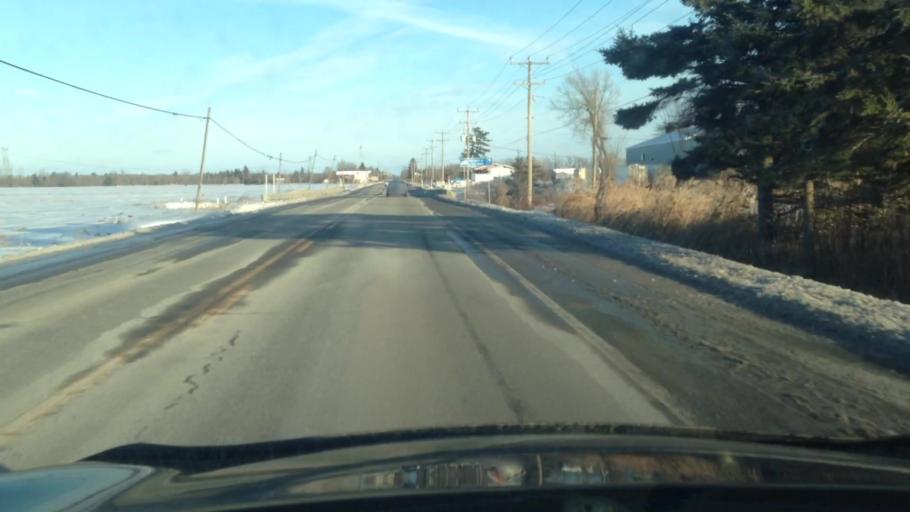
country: CA
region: Quebec
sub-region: Laurentides
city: Sainte-Sophie
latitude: 45.8342
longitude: -73.8658
